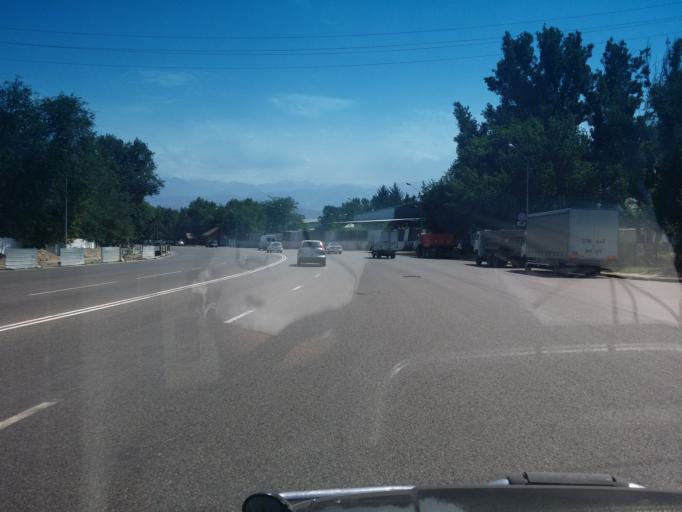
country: KZ
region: Almaty Oblysy
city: Pervomayskiy
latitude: 43.3454
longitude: 76.9711
